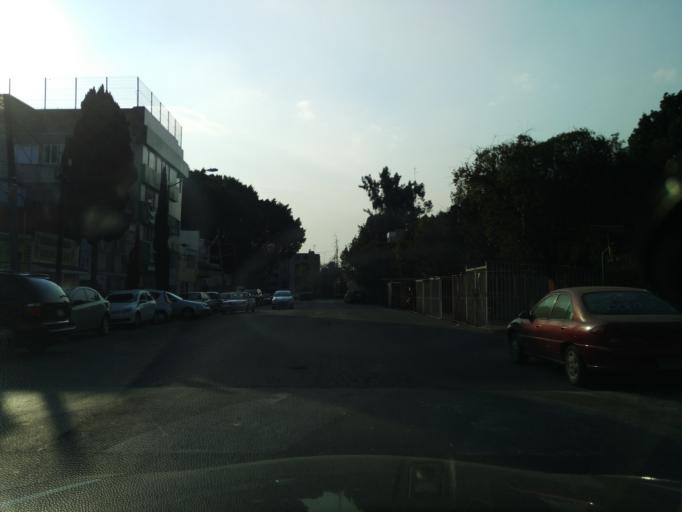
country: MX
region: Mexico City
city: Coyoacan
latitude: 19.3159
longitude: -99.1130
